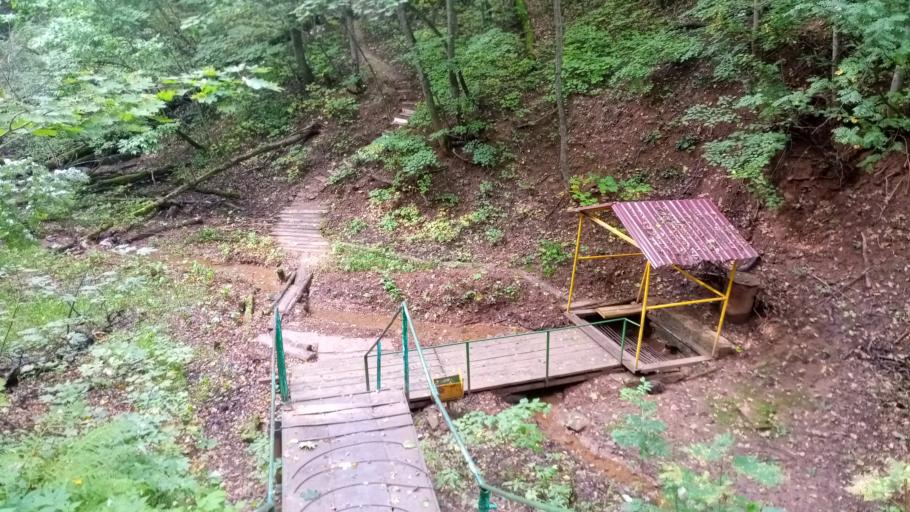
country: RU
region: Chuvashia
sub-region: Cheboksarskiy Rayon
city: Cheboksary
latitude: 56.1174
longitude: 47.2528
